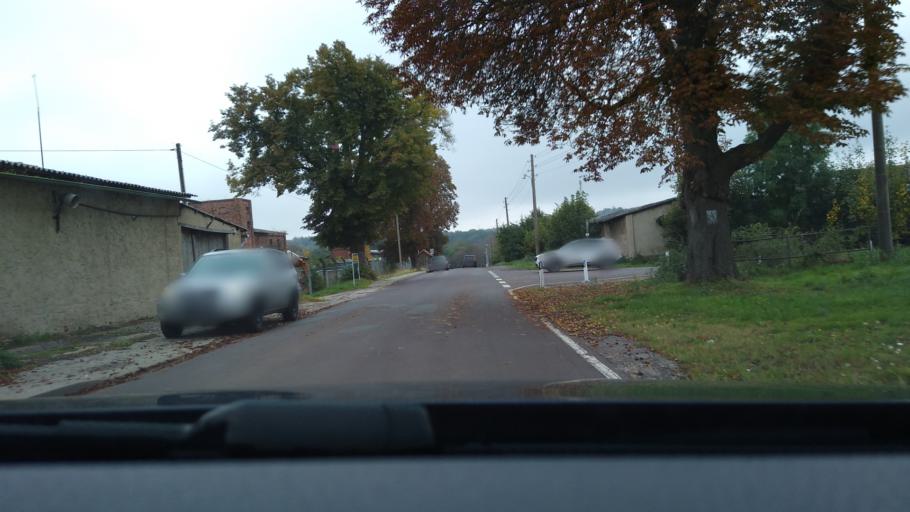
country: DE
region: Saxony-Anhalt
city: Gerbstedt
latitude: 51.6082
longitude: 11.6152
